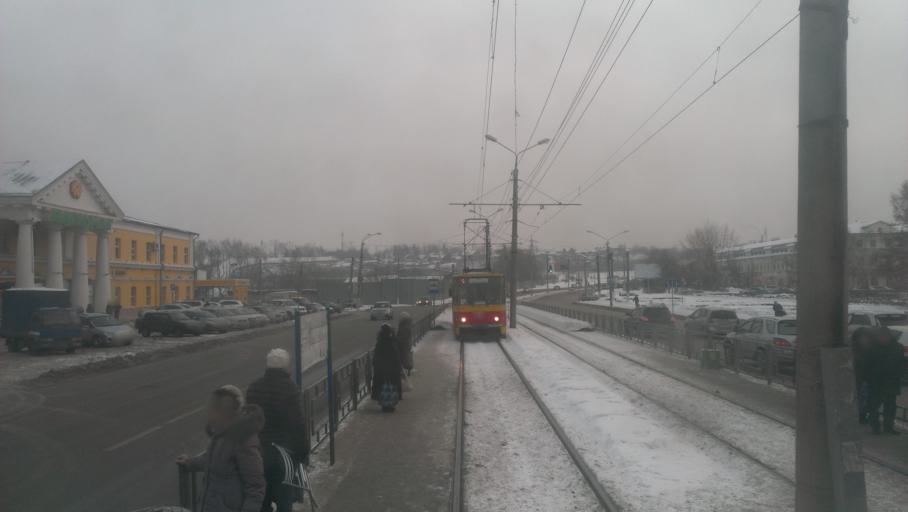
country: RU
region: Altai Krai
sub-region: Gorod Barnaulskiy
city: Barnaul
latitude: 53.3293
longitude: 83.7843
